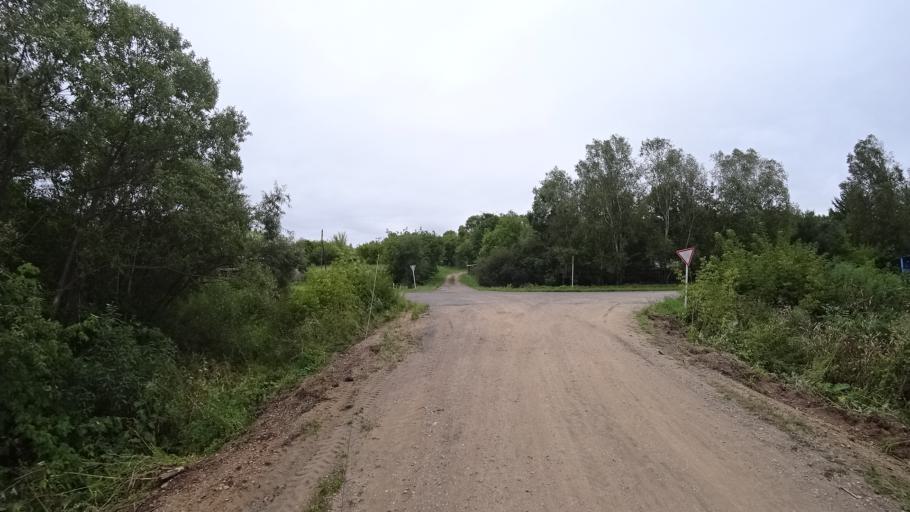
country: RU
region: Primorskiy
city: Rettikhovka
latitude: 44.1672
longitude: 132.7415
